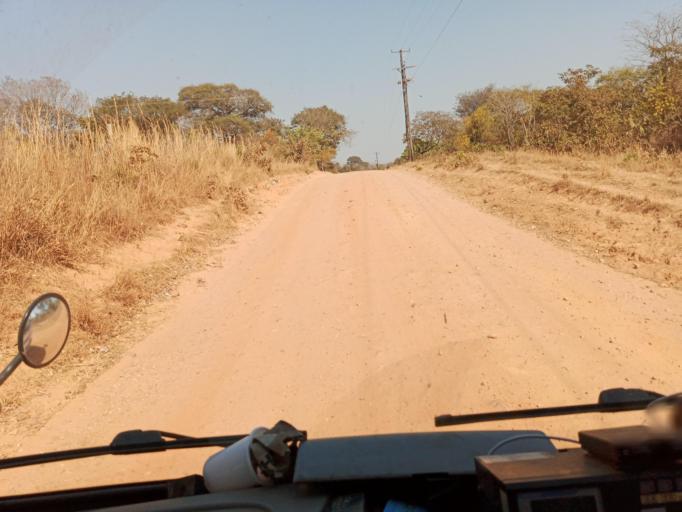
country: ZM
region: Lusaka
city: Lusaka
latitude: -15.3386
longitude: 28.1940
